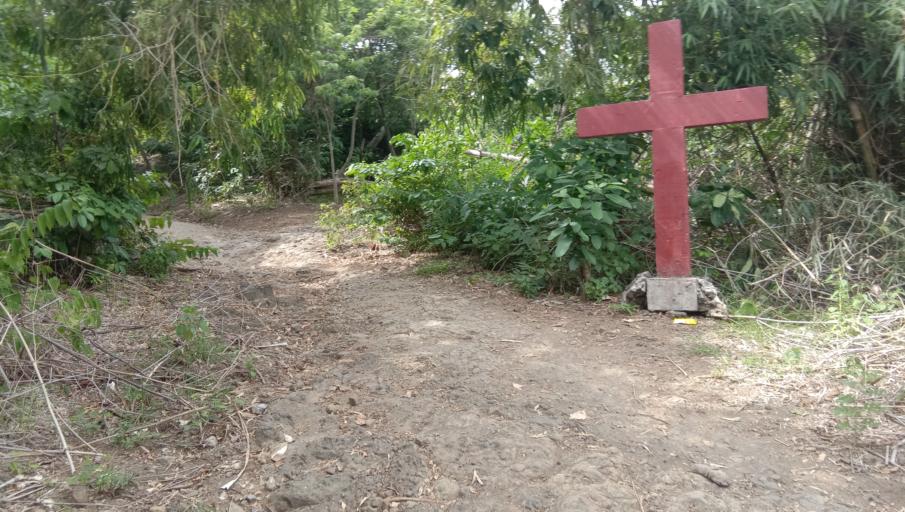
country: PH
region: Western Visayas
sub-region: Province of Capiz
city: Roxas City
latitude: 11.6076
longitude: 122.7068
